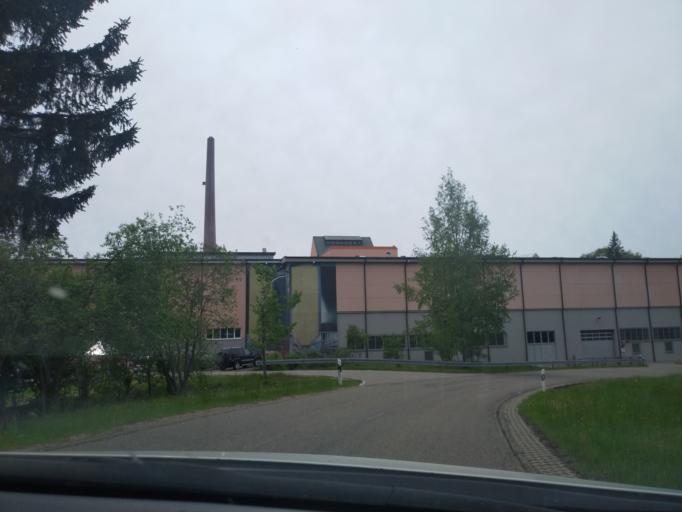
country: DE
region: Baden-Wuerttemberg
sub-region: Freiburg Region
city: Grafenhausen
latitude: 47.7971
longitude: 8.2442
